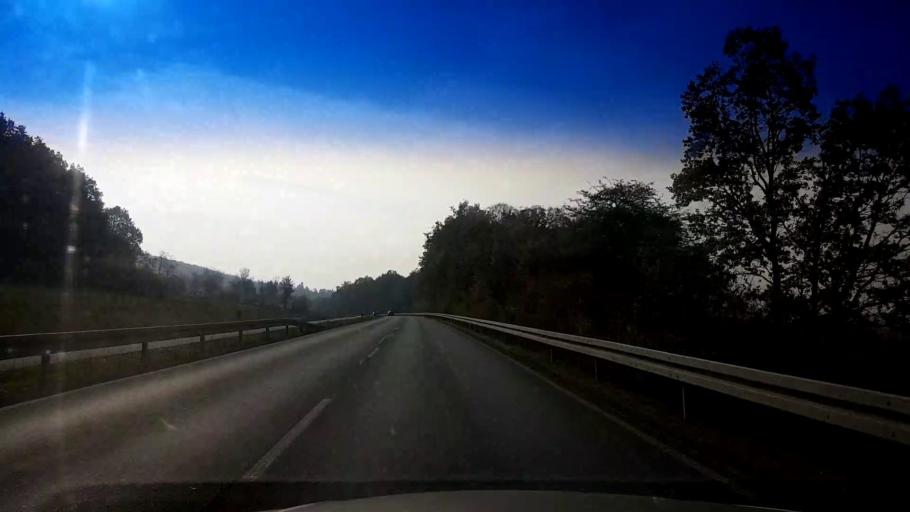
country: DE
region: Bavaria
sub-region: Upper Franconia
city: Neuenmarkt
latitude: 50.0950
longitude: 11.6067
